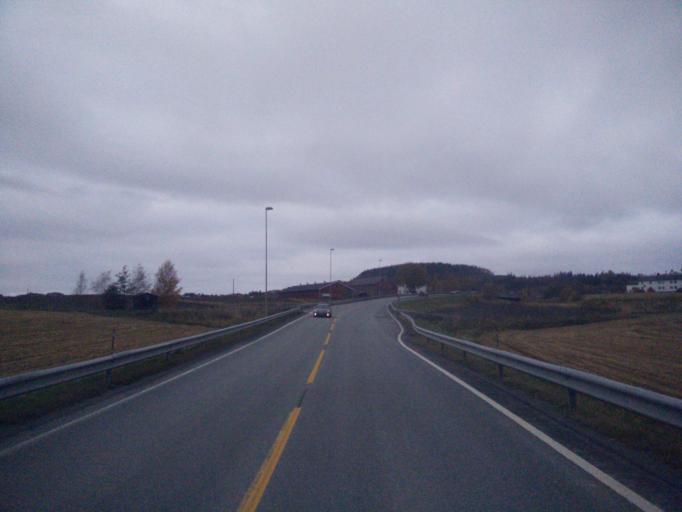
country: NO
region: Nord-Trondelag
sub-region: Stjordal
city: Stjordal
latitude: 63.5023
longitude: 10.8611
